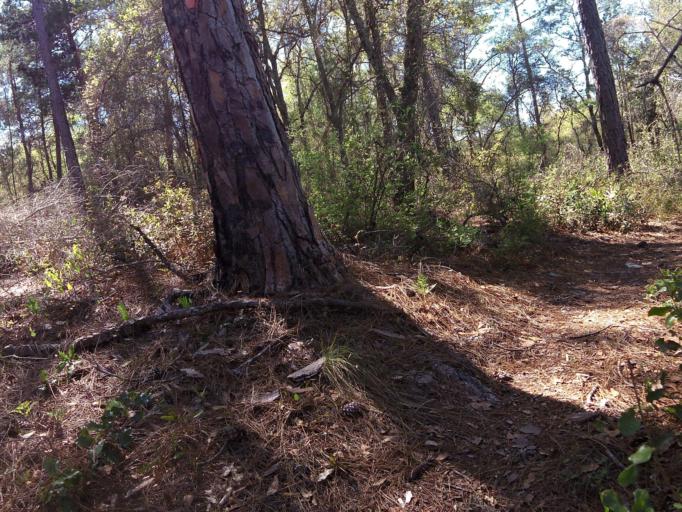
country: US
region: Florida
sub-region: Clay County
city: Keystone Heights
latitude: 29.8372
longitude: -81.9922
